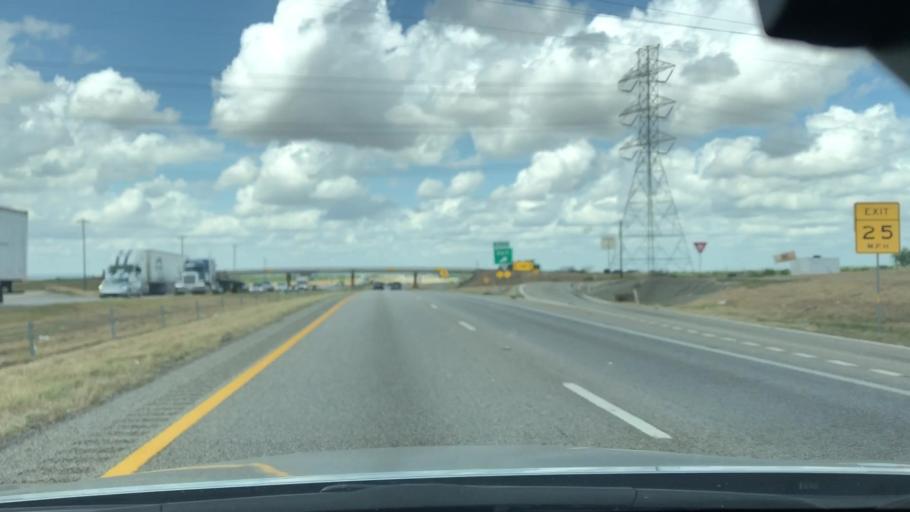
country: US
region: Texas
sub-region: Guadalupe County
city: Marion
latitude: 29.5371
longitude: -98.0829
